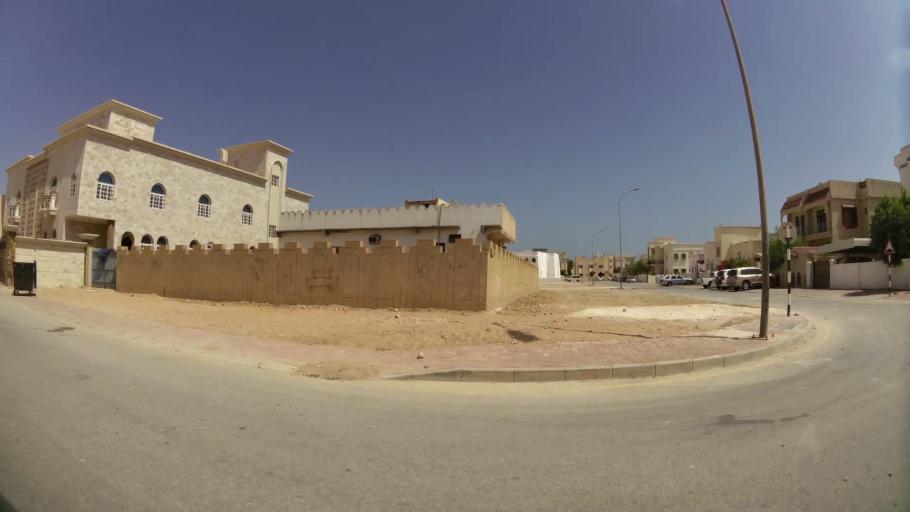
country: OM
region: Zufar
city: Salalah
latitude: 17.0416
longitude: 54.1523
